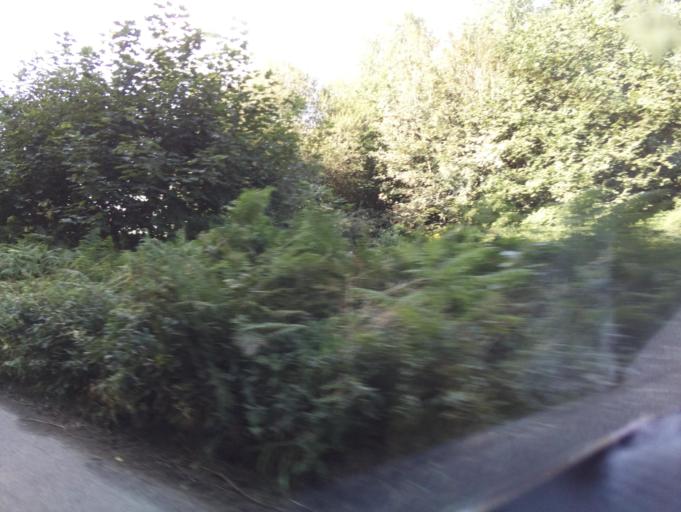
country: GB
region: England
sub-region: Devon
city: Buckfastleigh
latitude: 50.4431
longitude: -3.7901
